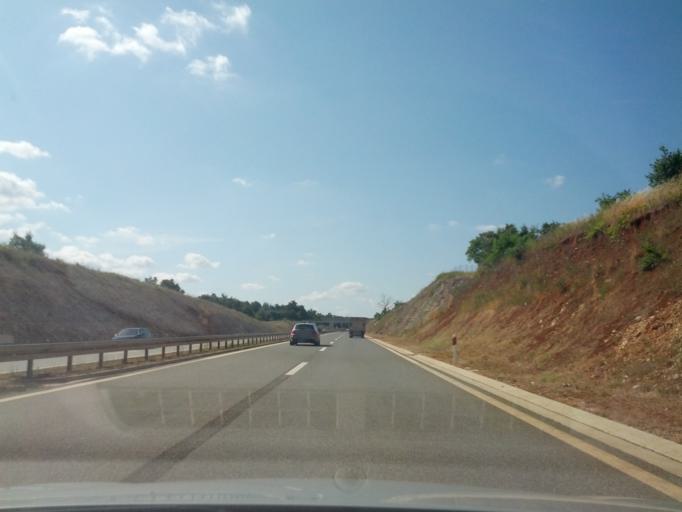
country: HR
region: Istarska
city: Karojba
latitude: 45.2094
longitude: 13.7264
